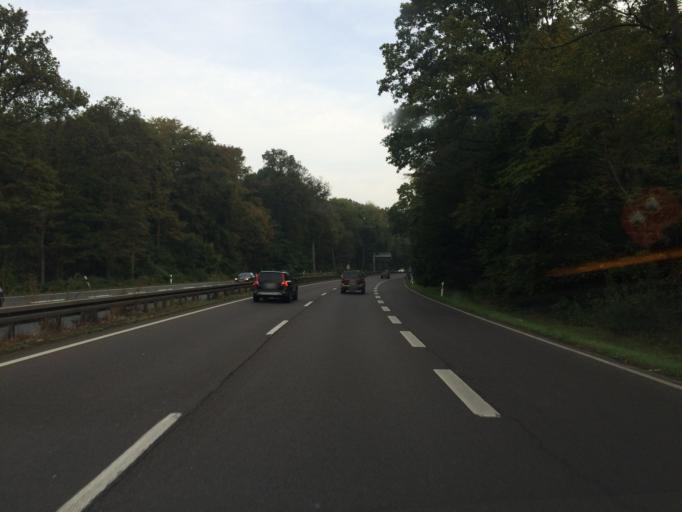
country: DE
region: Lower Saxony
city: Hannover
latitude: 52.3741
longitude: 9.7780
